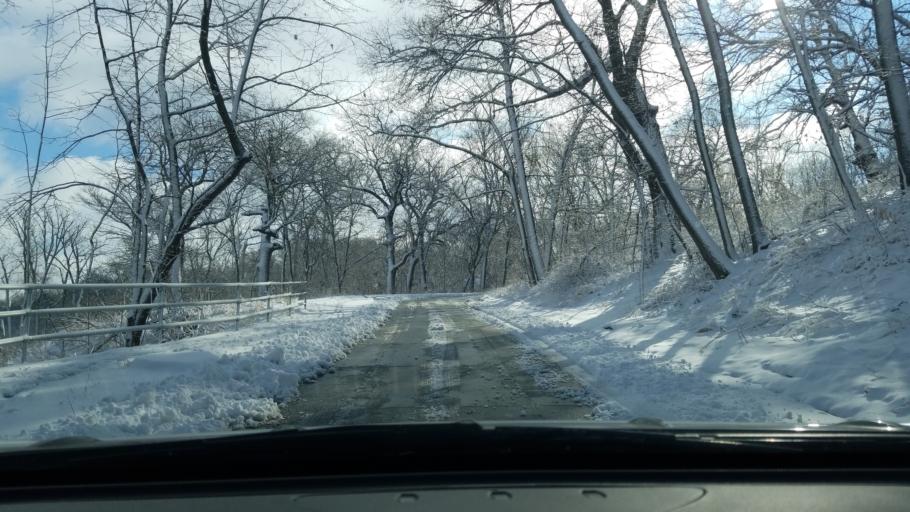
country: US
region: Nebraska
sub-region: Douglas County
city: Omaha
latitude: 41.2208
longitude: -95.9416
